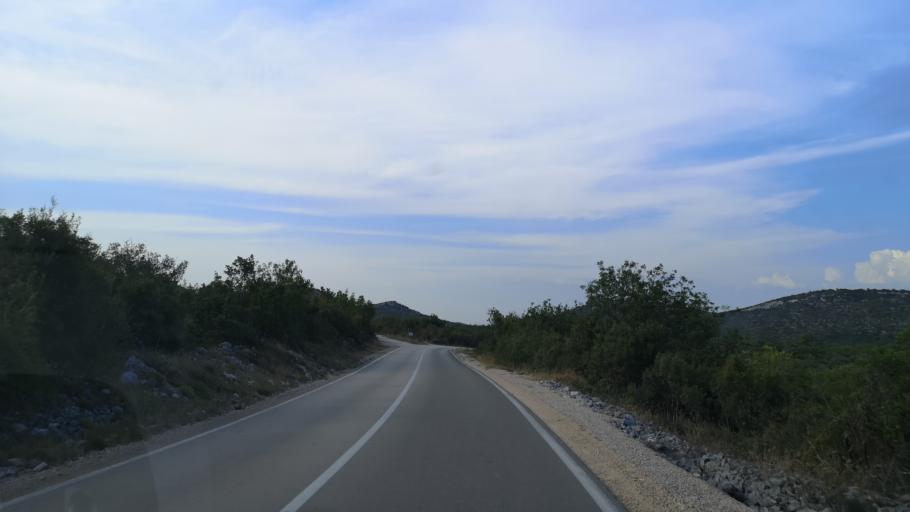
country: HR
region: Sibensko-Kniniska
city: Zaton
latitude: 43.8178
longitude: 15.7781
